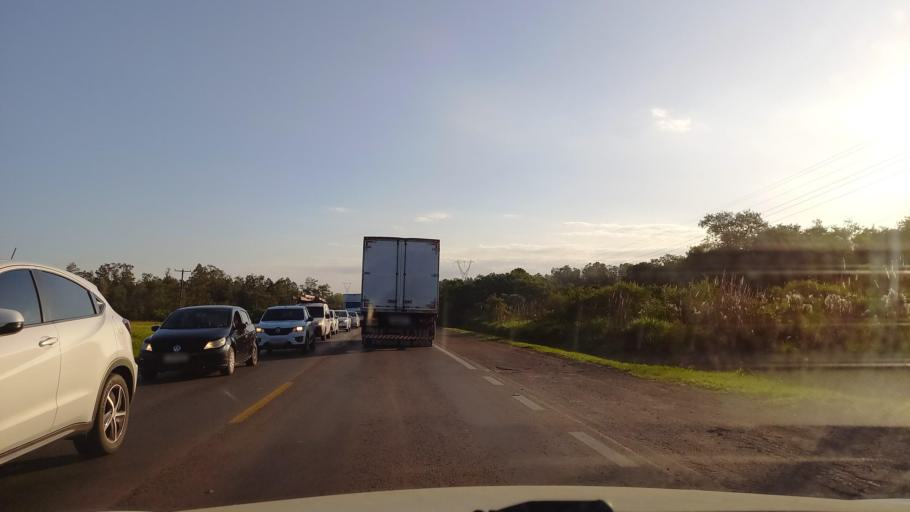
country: BR
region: Rio Grande do Sul
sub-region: Venancio Aires
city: Venancio Aires
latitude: -29.6396
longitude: -52.1625
